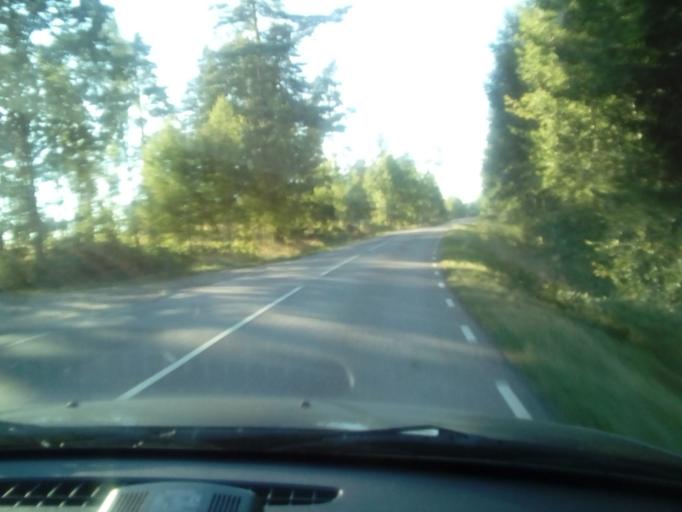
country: SE
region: Kalmar
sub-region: Vasterviks Kommun
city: Gamleby
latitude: 57.7911
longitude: 16.3808
